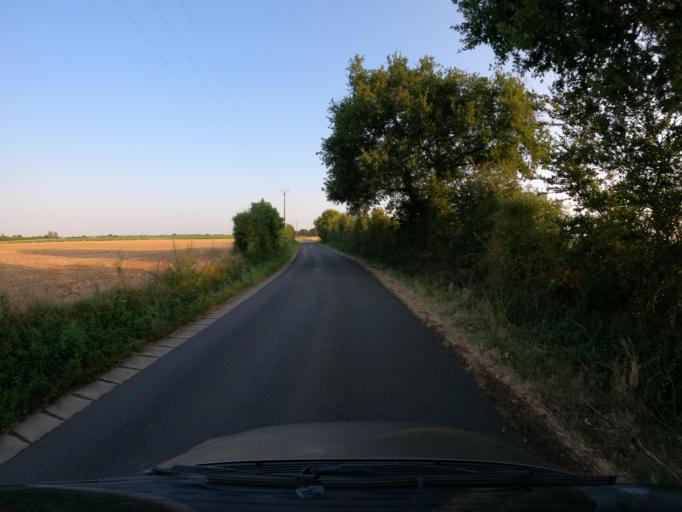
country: FR
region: Pays de la Loire
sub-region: Departement de la Sarthe
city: Parce-sur-Sarthe
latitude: 47.8967
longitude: -0.2191
